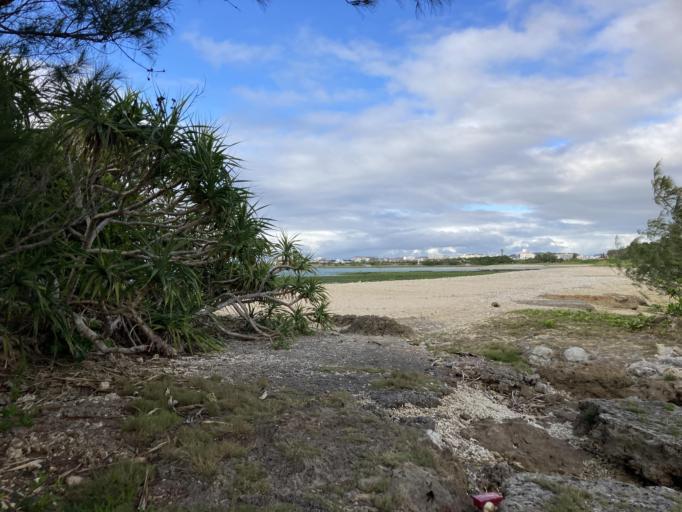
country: JP
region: Okinawa
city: Itoman
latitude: 26.1089
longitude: 127.6609
